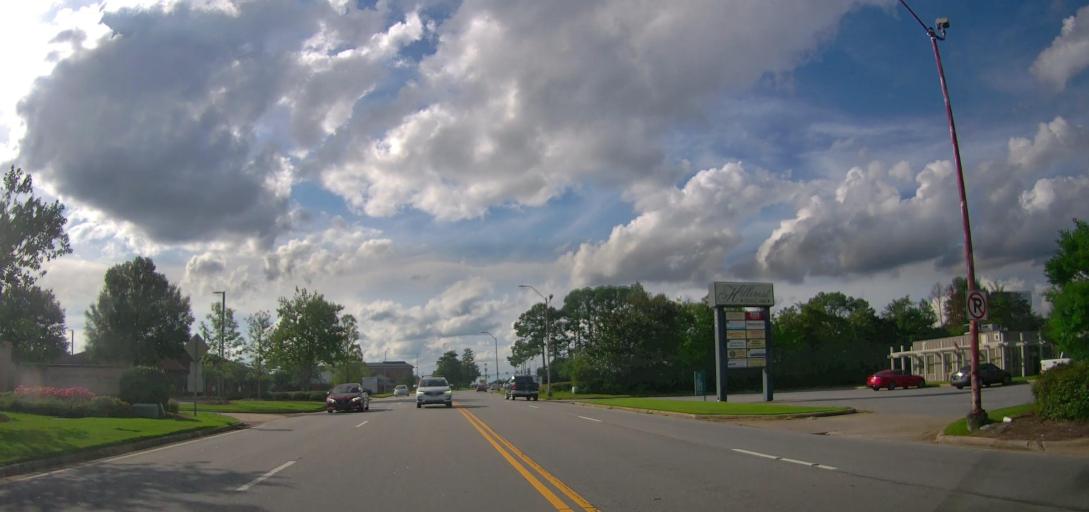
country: US
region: Alabama
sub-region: Russell County
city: Phenix City
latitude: 32.5241
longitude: -84.9594
